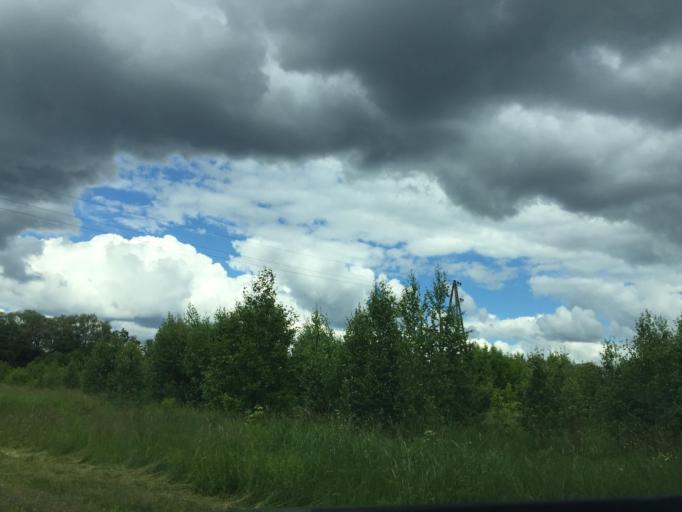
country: LV
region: Garkalne
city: Garkalne
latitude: 57.0745
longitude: 24.4004
